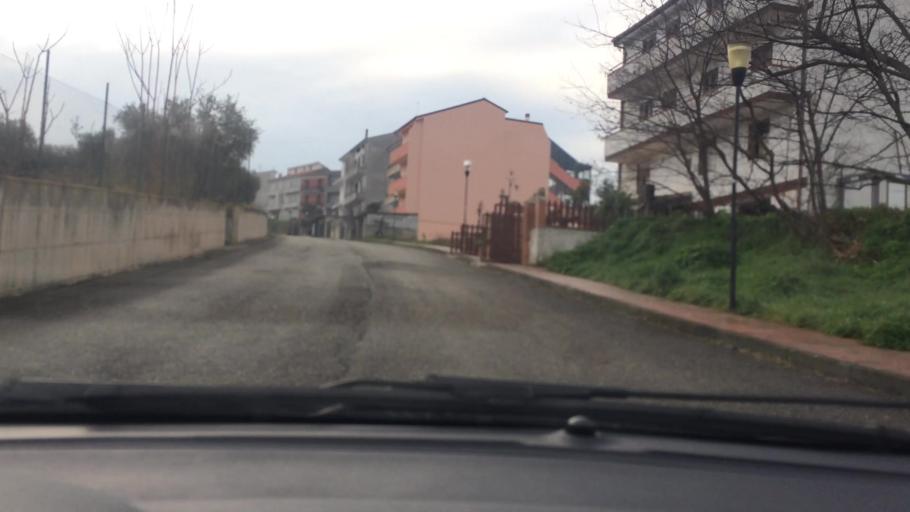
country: IT
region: Basilicate
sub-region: Provincia di Matera
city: San Mauro Forte
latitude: 40.4902
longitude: 16.2428
